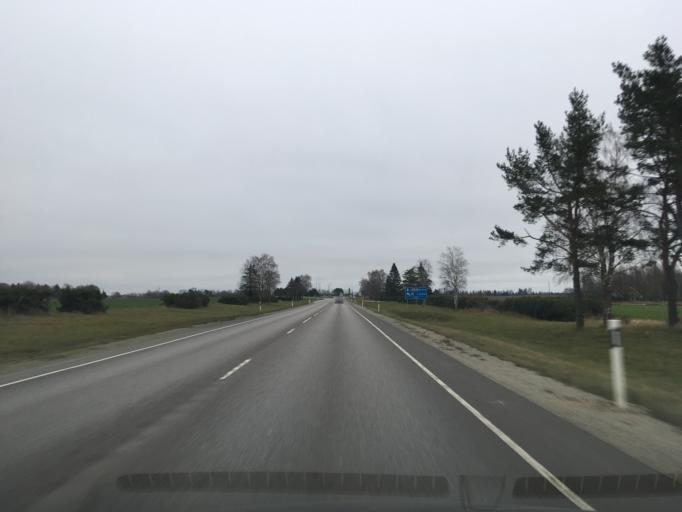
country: EE
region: Laeaene-Virumaa
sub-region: Haljala vald
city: Haljala
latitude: 59.4172
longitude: 26.3300
